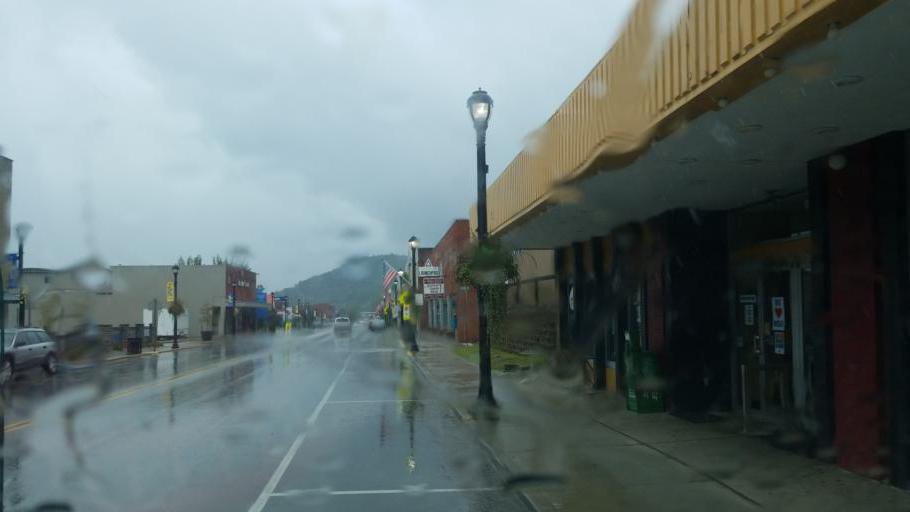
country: US
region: Kentucky
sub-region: Rowan County
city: Morehead
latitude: 38.1835
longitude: -83.4340
